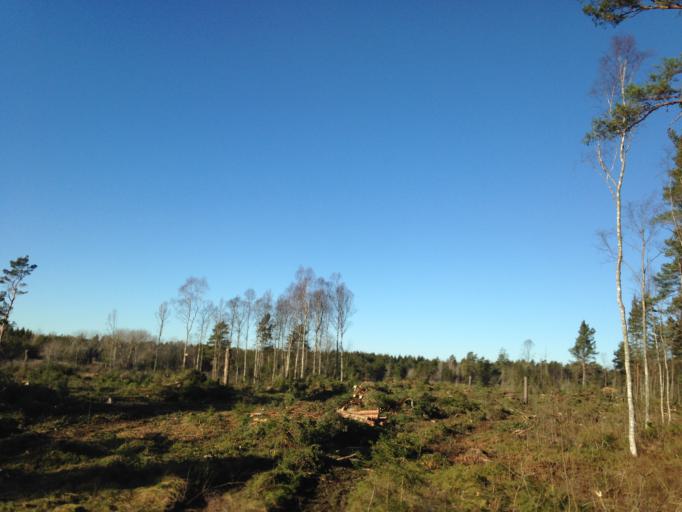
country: SE
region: Soedermanland
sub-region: Nykopings Kommun
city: Svalsta
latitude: 58.4854
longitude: 16.8793
